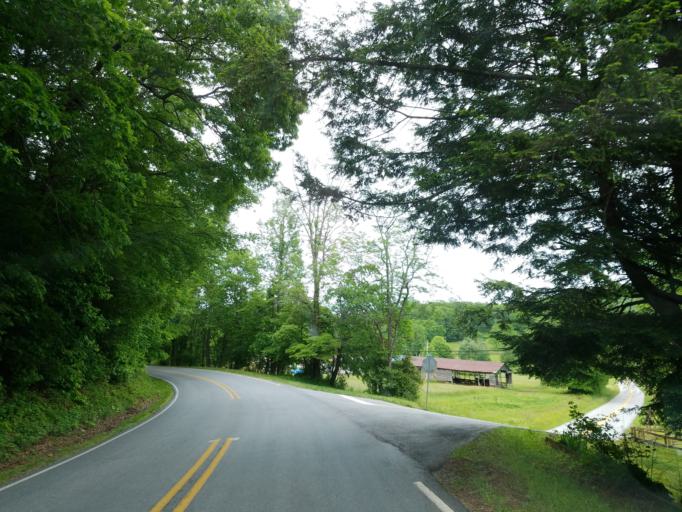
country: US
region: Georgia
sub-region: Lumpkin County
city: Dahlonega
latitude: 34.6982
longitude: -84.0135
